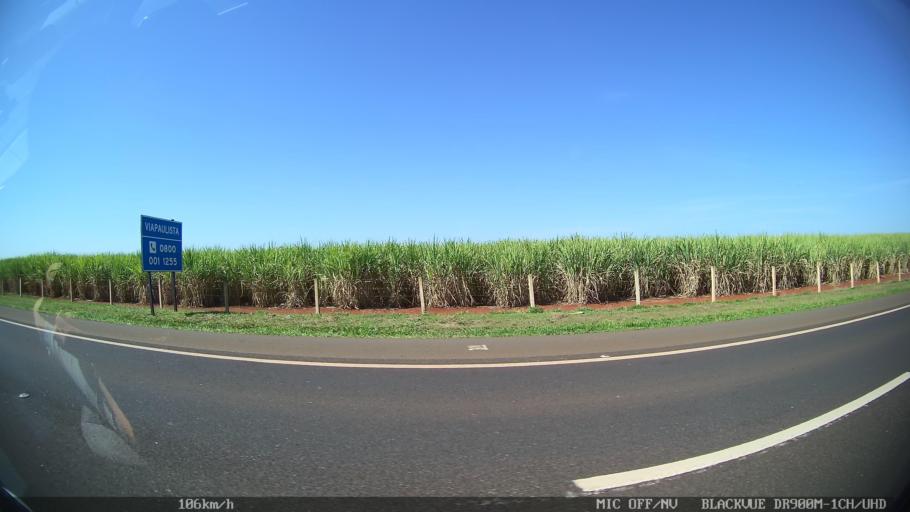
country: BR
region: Sao Paulo
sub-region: Batatais
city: Batatais
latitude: -20.7810
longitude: -47.5505
